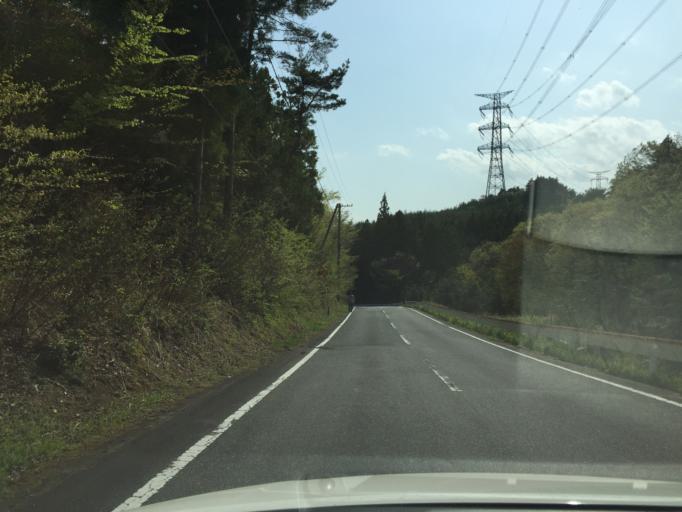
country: JP
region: Fukushima
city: Iwaki
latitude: 37.1649
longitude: 140.8551
